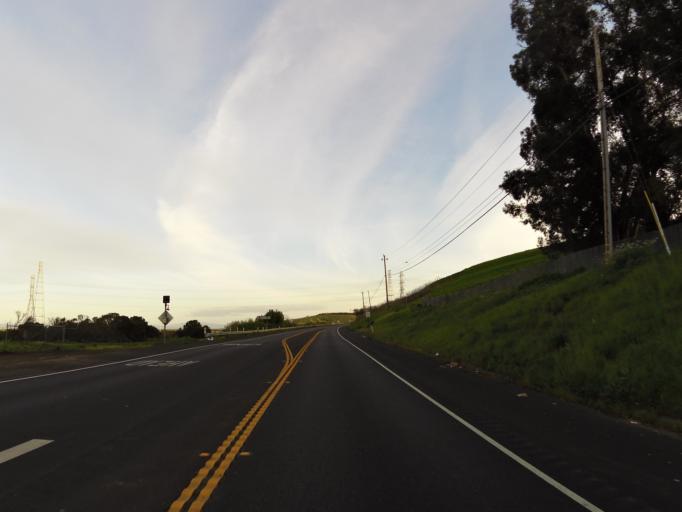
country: US
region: California
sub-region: Marin County
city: Black Point-Green Point
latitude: 38.1569
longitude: -122.4496
